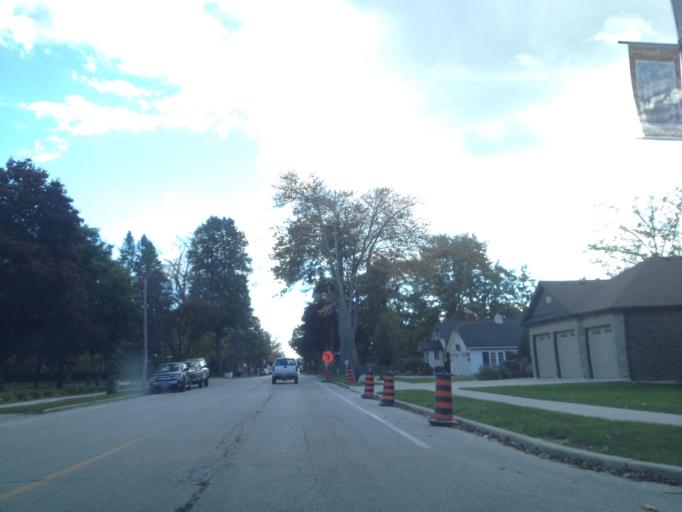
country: CA
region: Ontario
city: Amherstburg
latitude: 42.0300
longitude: -82.7403
